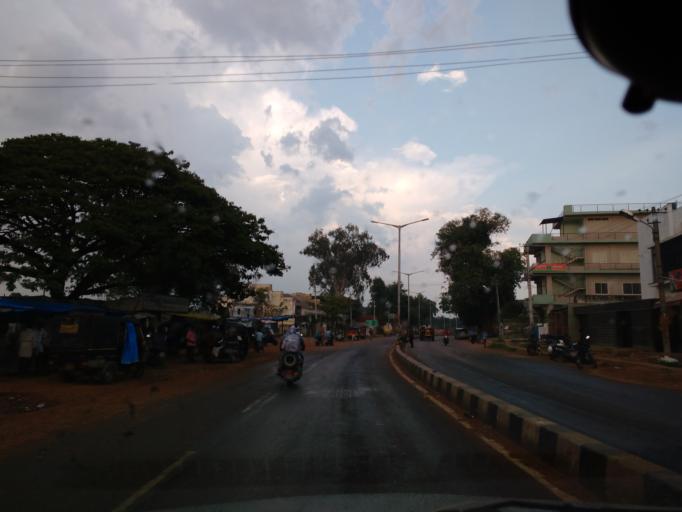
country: IN
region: Karnataka
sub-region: Tumkur
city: Tiptur
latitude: 13.2594
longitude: 76.4801
